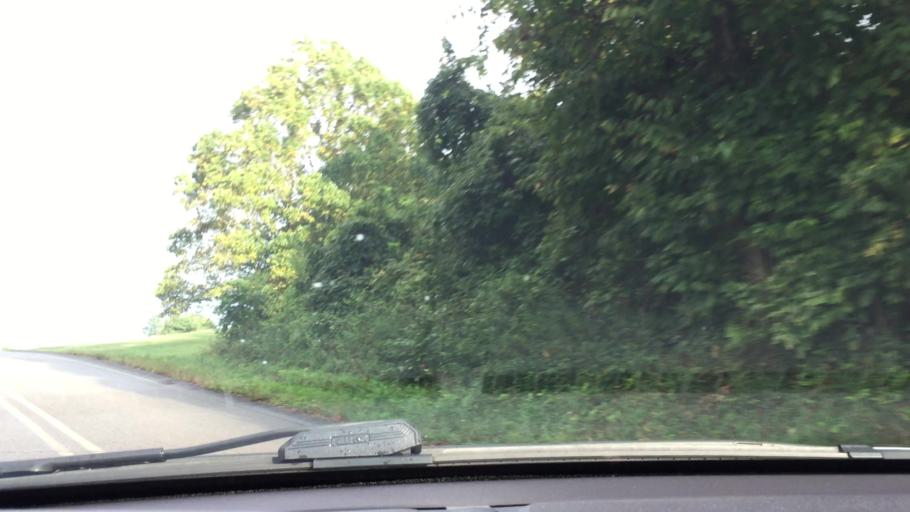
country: US
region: Pennsylvania
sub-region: Washington County
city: McGovern
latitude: 40.2078
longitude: -80.1858
